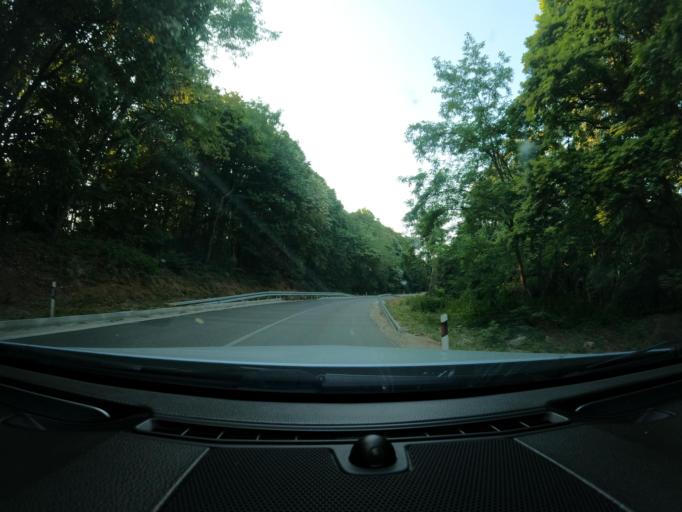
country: RS
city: Vrdnik
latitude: 45.1353
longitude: 19.7239
